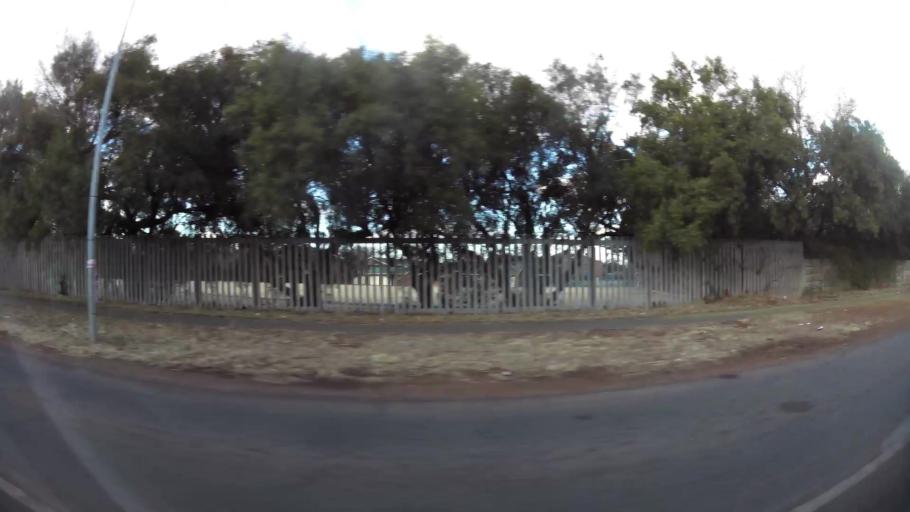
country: ZA
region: North-West
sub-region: Dr Kenneth Kaunda District Municipality
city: Potchefstroom
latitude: -26.7152
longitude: 27.0875
